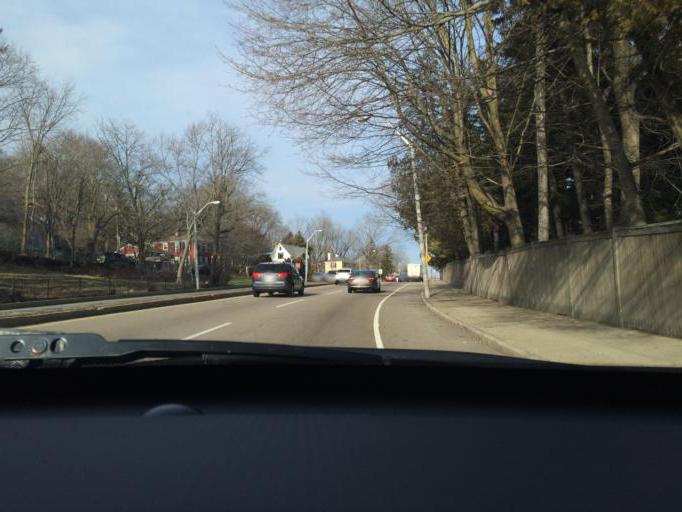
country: US
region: Massachusetts
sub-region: Suffolk County
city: Jamaica Plain
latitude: 42.3050
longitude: -71.1246
